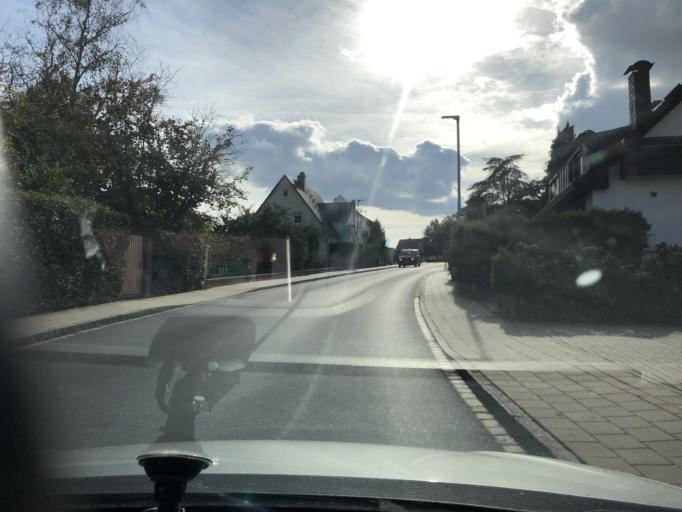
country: DE
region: Bavaria
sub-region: Regierungsbezirk Mittelfranken
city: Seukendorf
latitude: 49.4574
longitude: 10.8876
